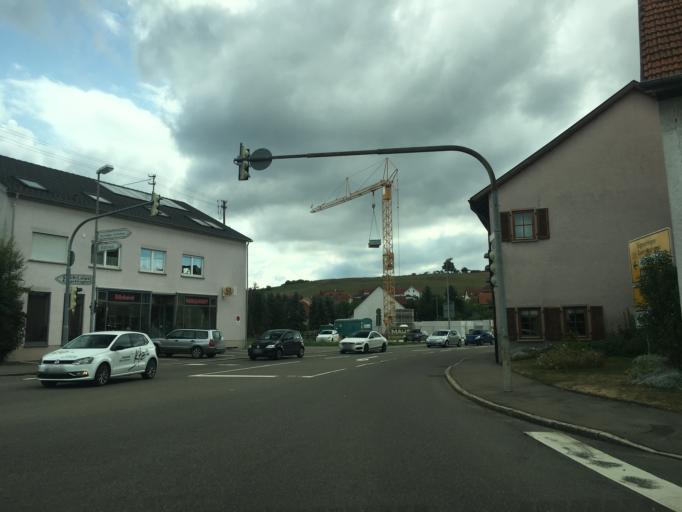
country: DE
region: Baden-Wuerttemberg
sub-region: Tuebingen Region
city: Trochtelfingen
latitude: 48.3870
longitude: 9.2858
